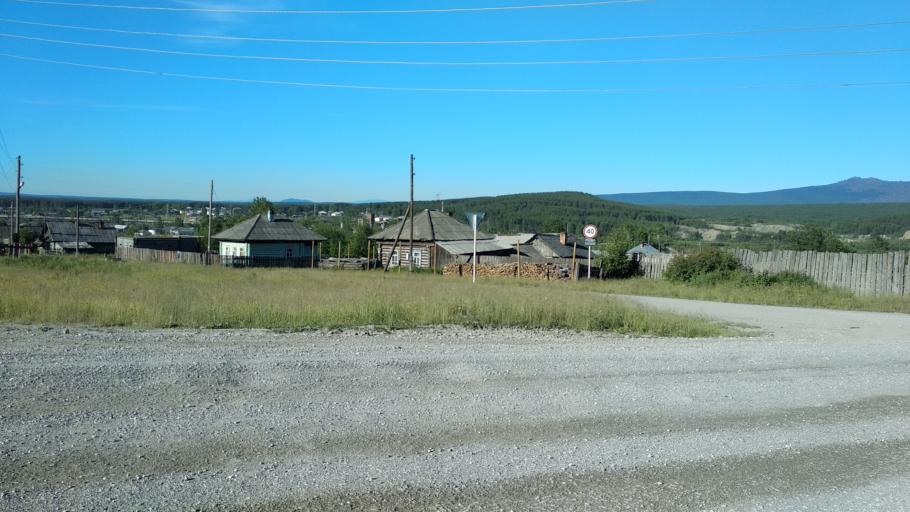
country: RU
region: Sverdlovsk
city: Severoural'sk
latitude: 60.1536
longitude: 59.8295
